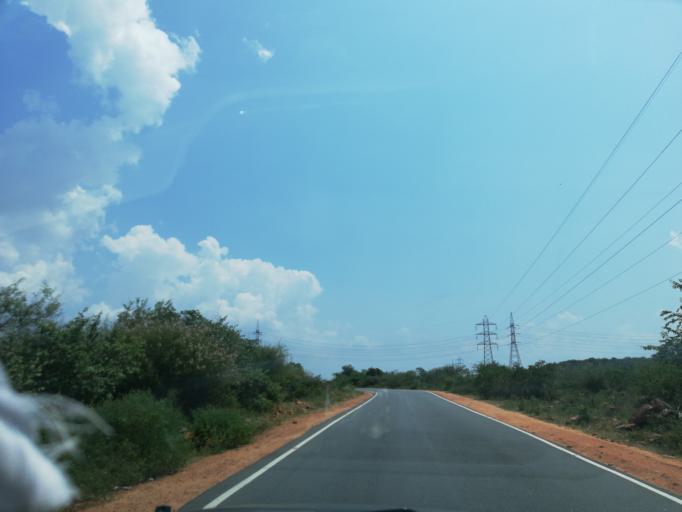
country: IN
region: Andhra Pradesh
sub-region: Guntur
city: Macherla
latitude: 16.5667
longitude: 79.3368
